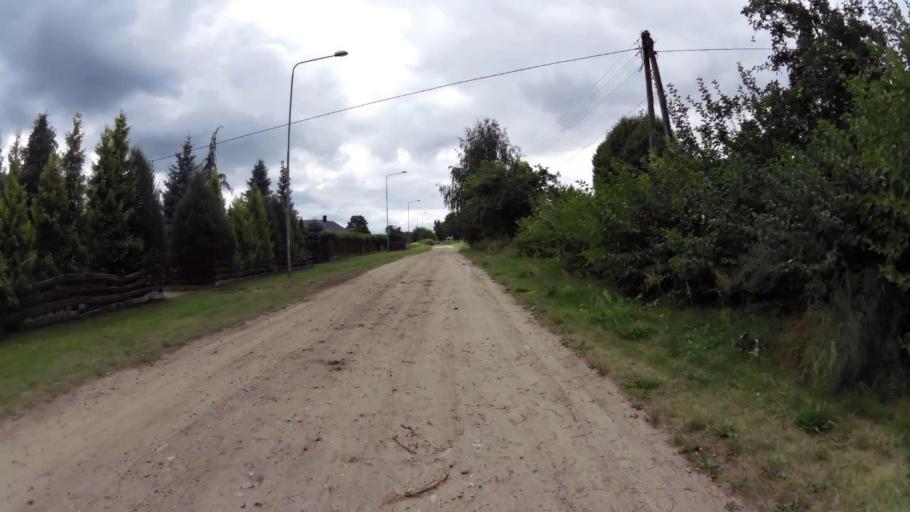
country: PL
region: West Pomeranian Voivodeship
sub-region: Powiat mysliborski
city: Debno
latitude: 52.7598
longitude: 14.7072
